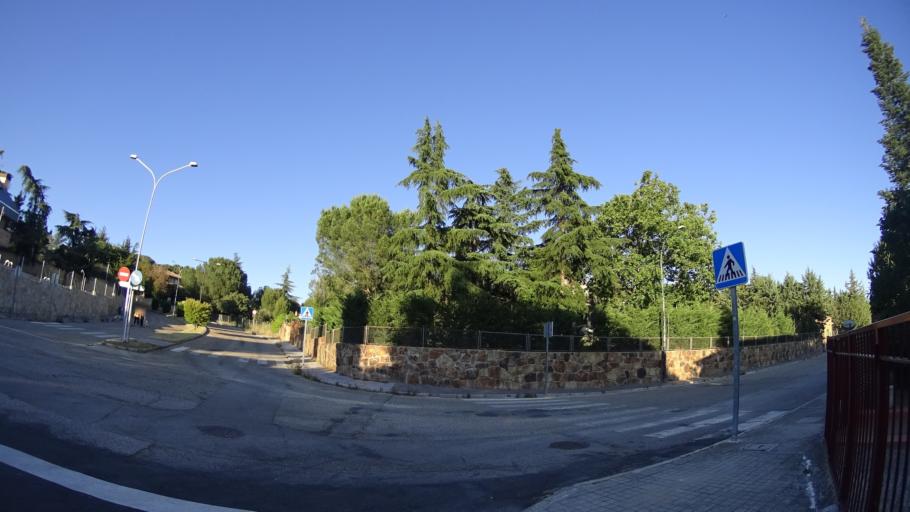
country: ES
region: Madrid
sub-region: Provincia de Madrid
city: Galapagar
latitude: 40.5934
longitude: -3.9684
